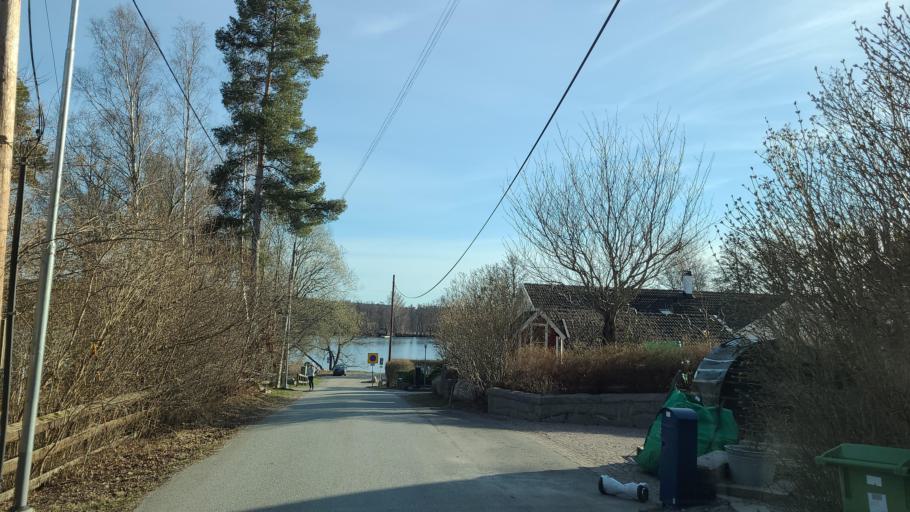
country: SE
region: Stockholm
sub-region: Ekero Kommun
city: Ekeroe
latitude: 59.2695
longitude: 17.8051
